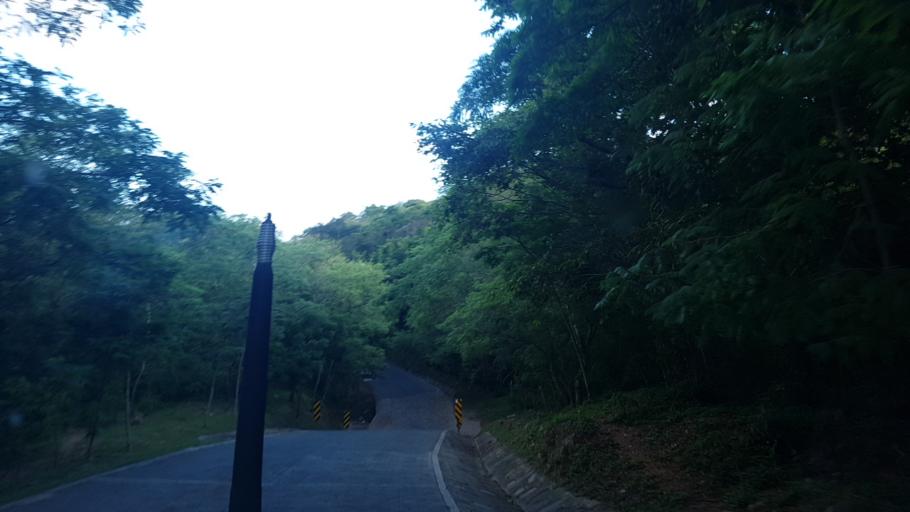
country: NI
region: Nueva Segovia
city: Ocotal
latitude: 13.6486
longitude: -86.6083
